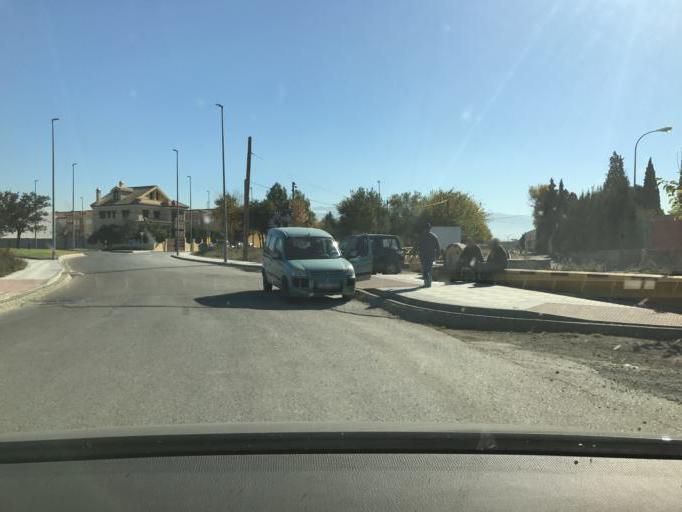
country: ES
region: Andalusia
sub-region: Provincia de Granada
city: Maracena
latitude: 37.2088
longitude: -3.6470
